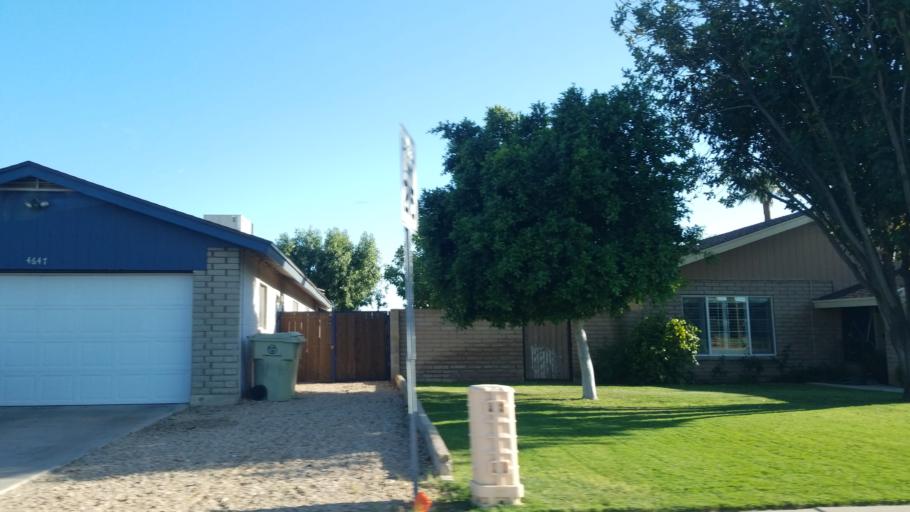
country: US
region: Arizona
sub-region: Maricopa County
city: Glendale
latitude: 33.5424
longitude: -112.1597
